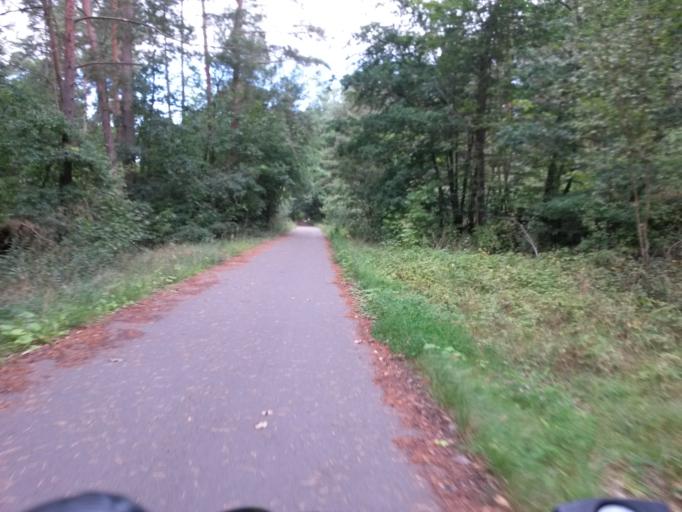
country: DE
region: Brandenburg
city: Templin
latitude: 53.1385
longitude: 13.5453
